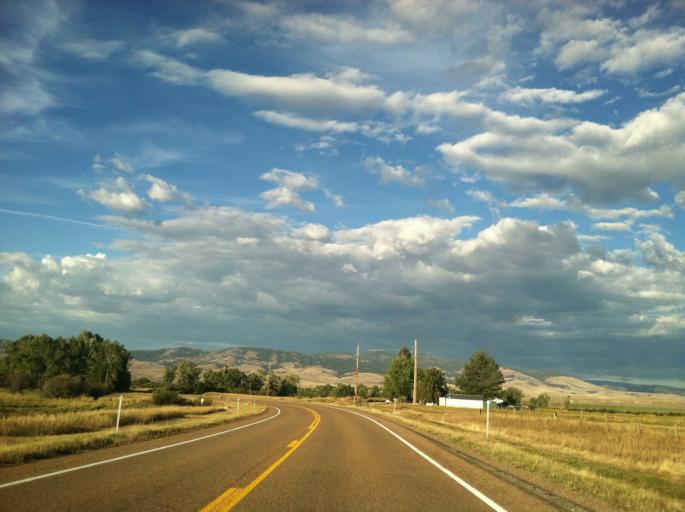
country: US
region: Montana
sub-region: Granite County
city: Philipsburg
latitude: 46.6104
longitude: -113.1802
